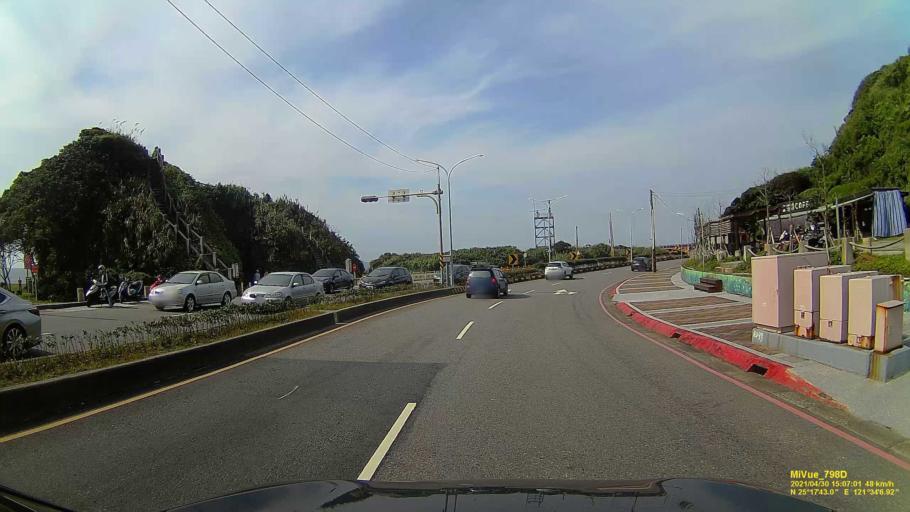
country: TW
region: Taiwan
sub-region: Keelung
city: Keelung
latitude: 25.2954
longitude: 121.5687
